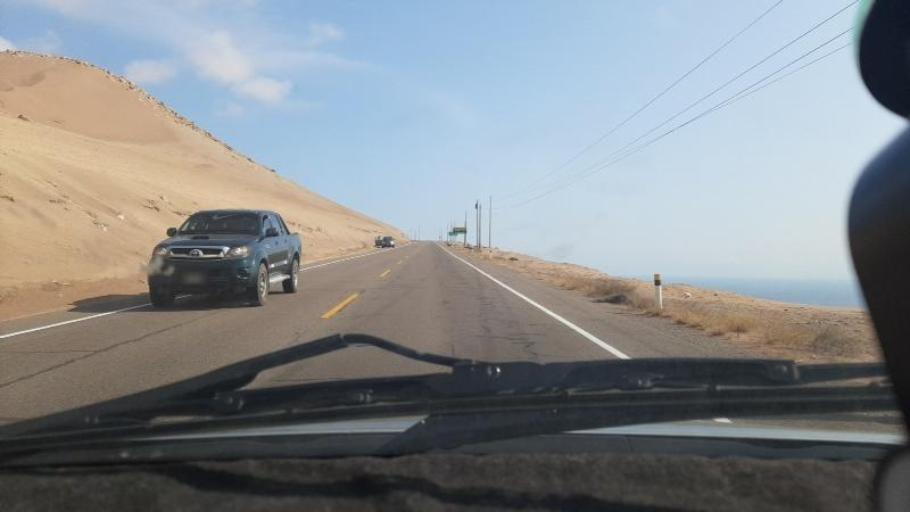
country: PE
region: Moquegua
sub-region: Provincia de Ilo
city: Ilo
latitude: -17.6751
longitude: -71.2931
